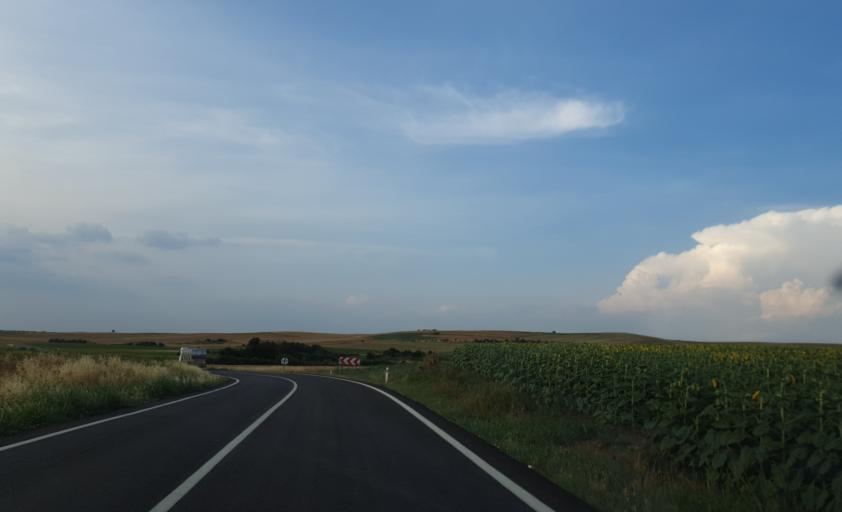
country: TR
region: Tekirdag
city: Hayrabolu
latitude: 41.2497
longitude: 27.1375
